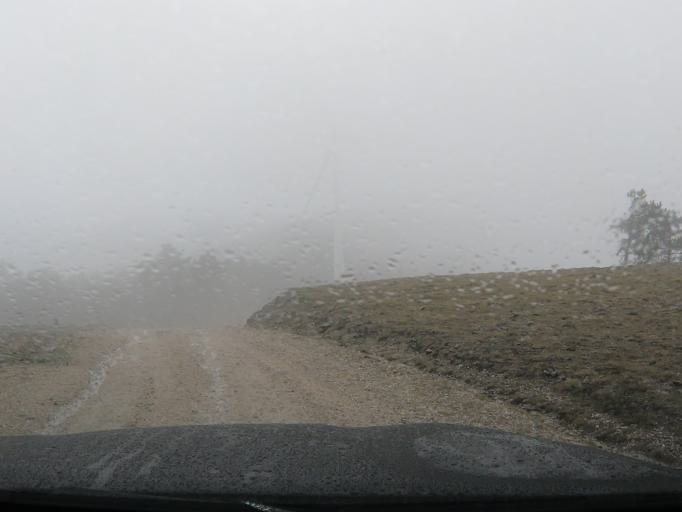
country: PT
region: Vila Real
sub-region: Mondim de Basto
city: Mondim de Basto
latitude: 41.3192
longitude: -7.8845
